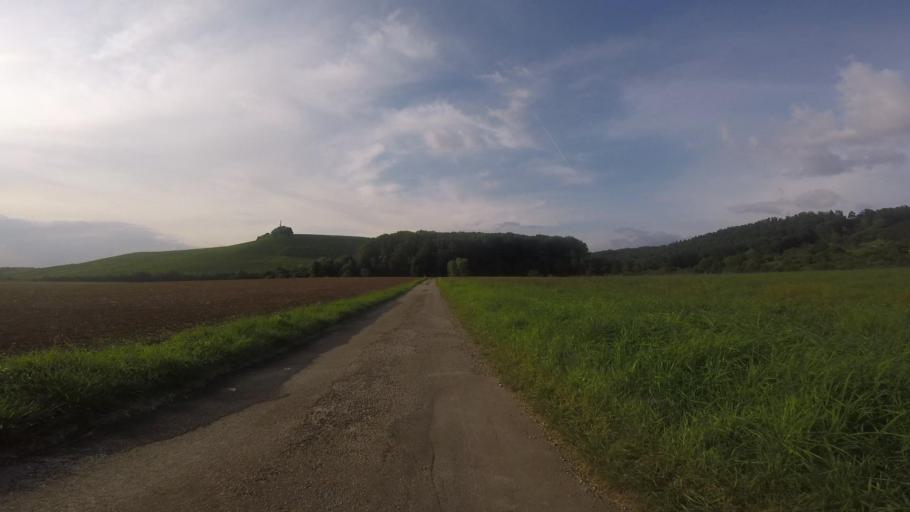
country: DE
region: Baden-Wuerttemberg
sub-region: Regierungsbezirk Stuttgart
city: Aspach
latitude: 48.9958
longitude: 9.3817
